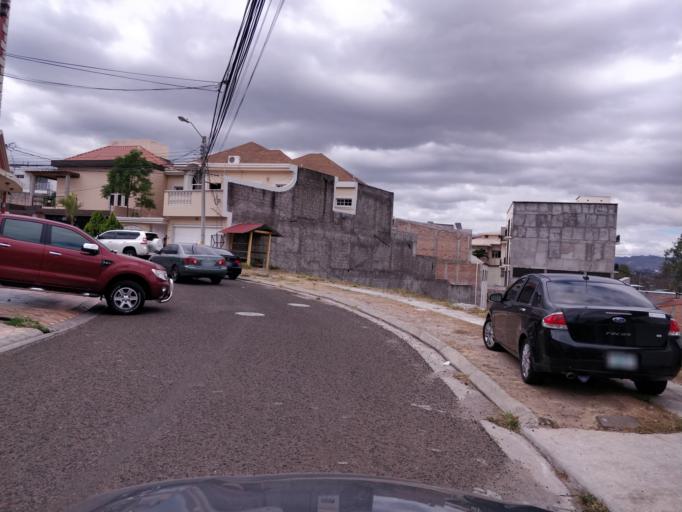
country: HN
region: Francisco Morazan
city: Yaguacire
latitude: 14.0499
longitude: -87.2166
